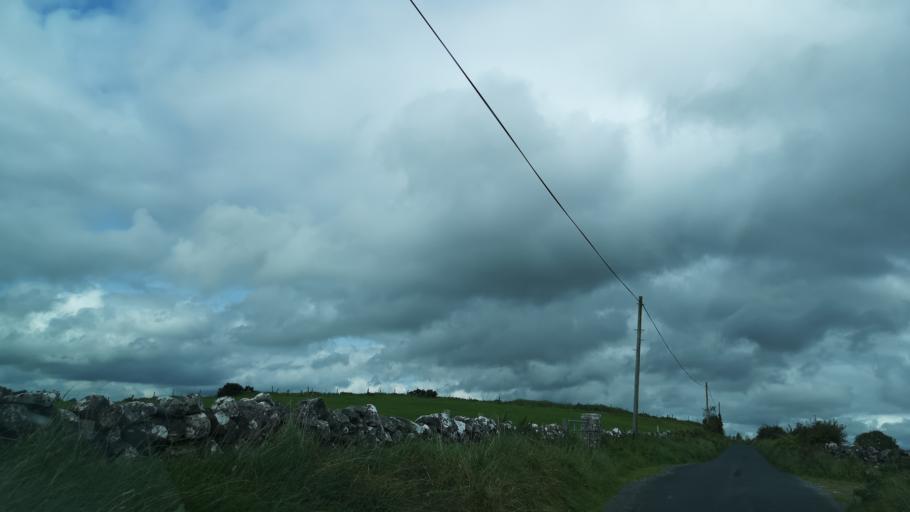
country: IE
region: Connaught
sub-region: County Galway
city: Athenry
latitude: 53.2793
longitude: -8.6700
